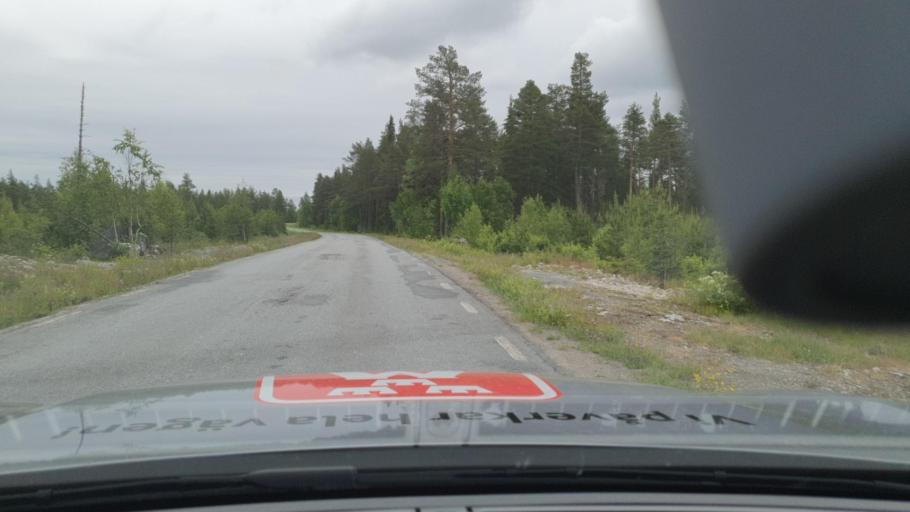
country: SE
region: Norrbotten
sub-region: Lulea Kommun
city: Ranea
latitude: 65.8368
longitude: 22.3026
